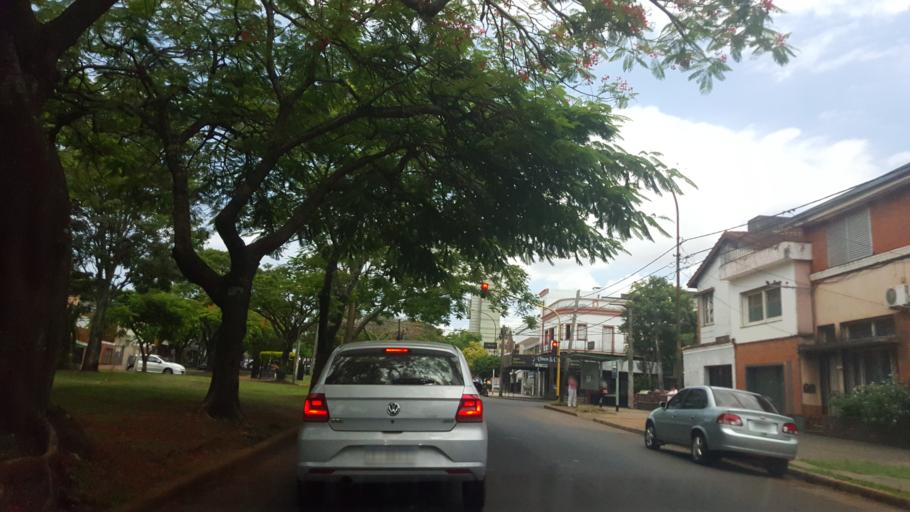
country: AR
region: Misiones
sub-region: Departamento de Capital
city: Posadas
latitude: -27.3745
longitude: -55.8952
